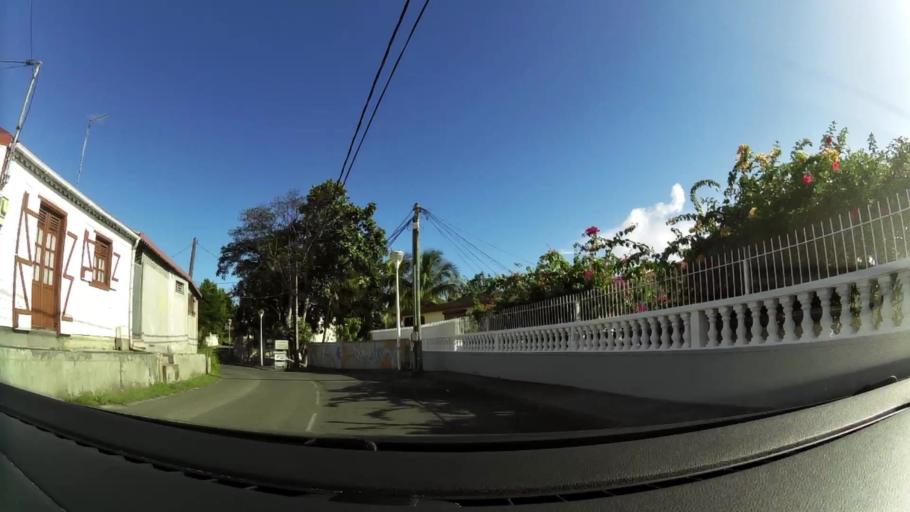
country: GP
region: Guadeloupe
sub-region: Guadeloupe
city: Le Gosier
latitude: 16.2061
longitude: -61.4821
